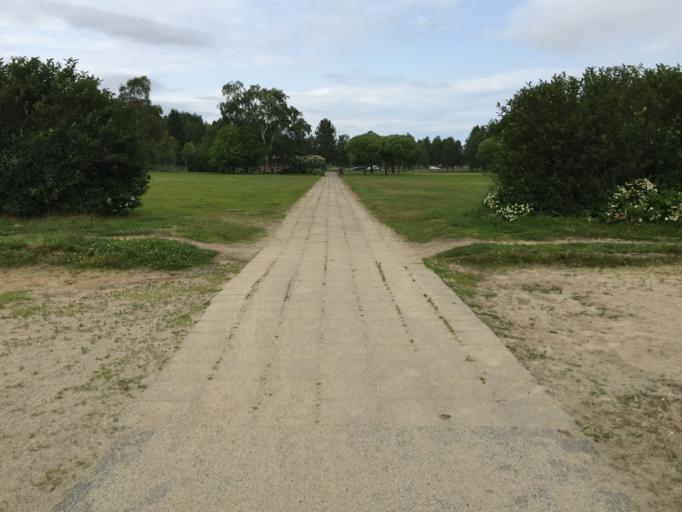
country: SE
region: Vaesterbotten
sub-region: Umea Kommun
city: Ersmark
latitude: 63.8364
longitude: 20.3399
